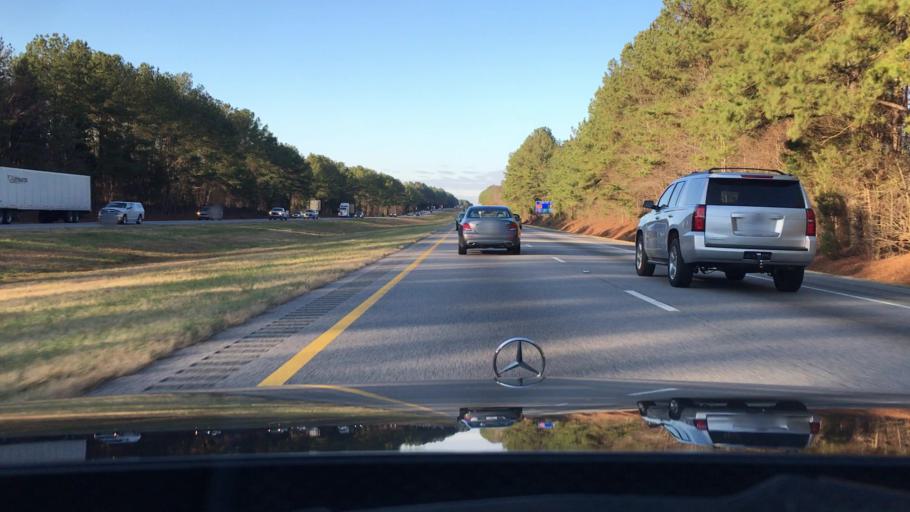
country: US
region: South Carolina
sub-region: Chester County
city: Eureka Mill
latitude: 34.7279
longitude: -81.0333
